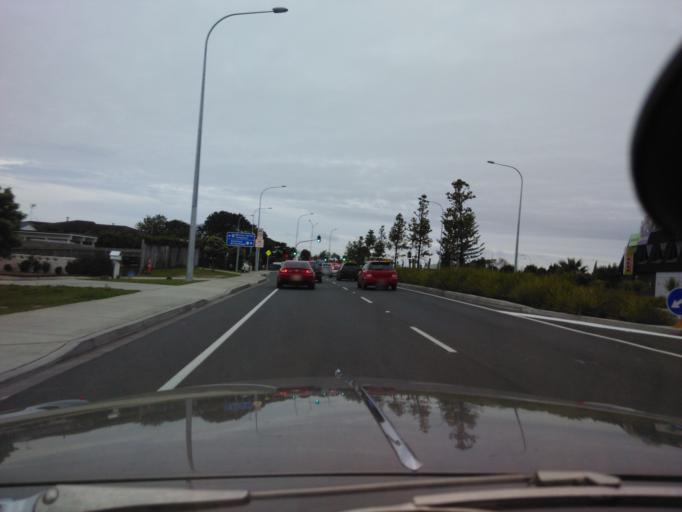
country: NZ
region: Auckland
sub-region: Auckland
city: North Shore
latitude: -36.7689
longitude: 174.7209
